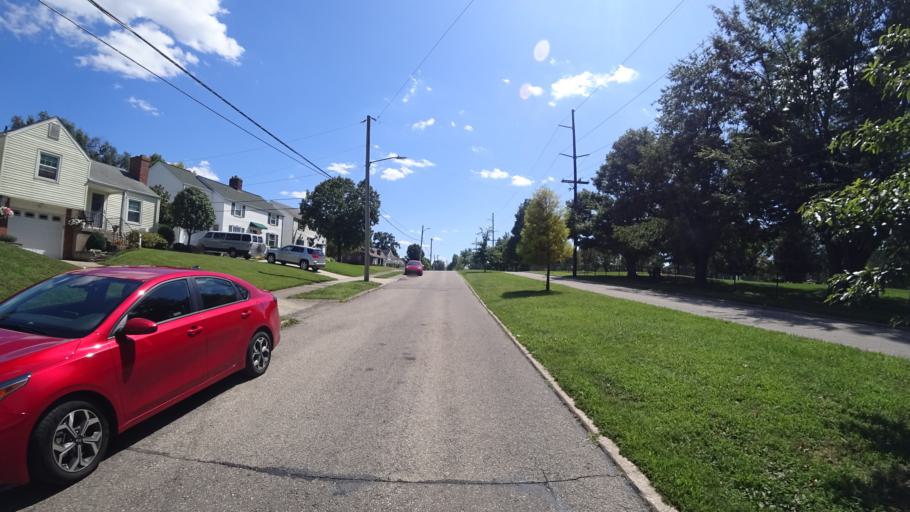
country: US
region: Ohio
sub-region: Butler County
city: Hamilton
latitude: 39.4083
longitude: -84.5382
